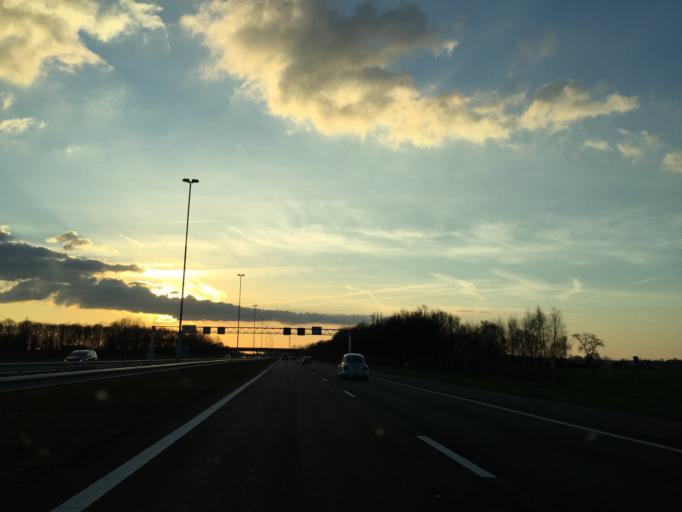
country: NL
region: North Brabant
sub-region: Gemeente Dongen
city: Dongen
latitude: 51.5567
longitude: 4.9001
